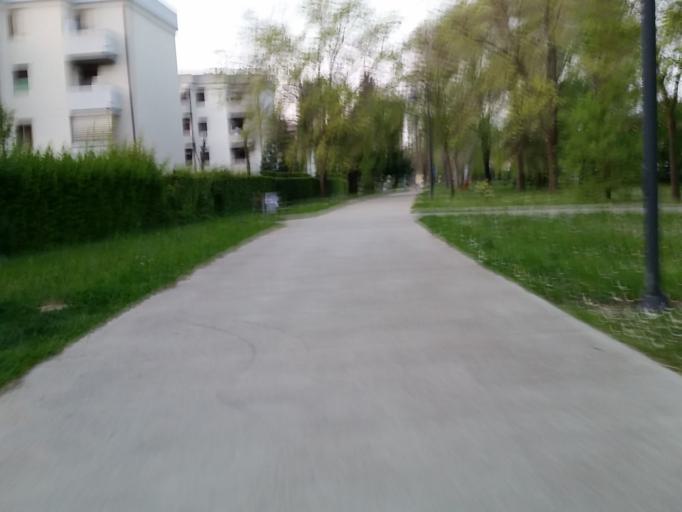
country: IT
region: Veneto
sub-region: Provincia di Padova
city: Mandriola-Sant'Agostino
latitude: 45.3636
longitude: 11.8468
